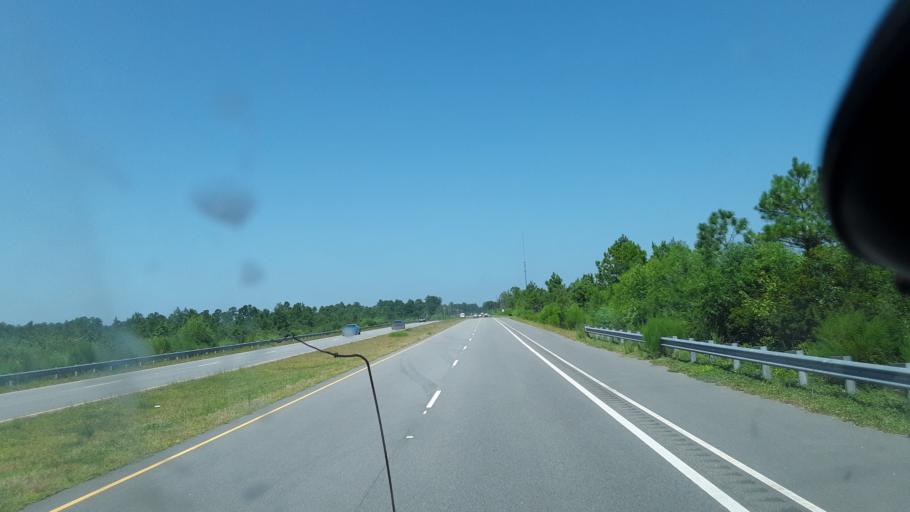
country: US
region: South Carolina
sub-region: Horry County
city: Forestbrook
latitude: 33.8101
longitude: -78.8972
